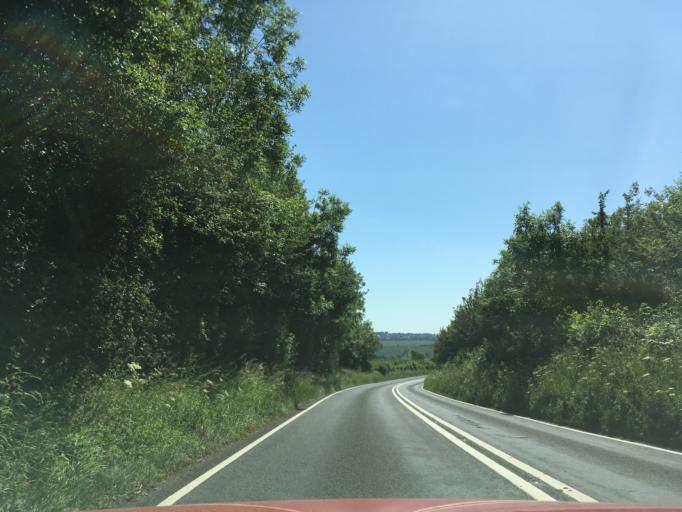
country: GB
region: England
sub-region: Oxfordshire
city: Chipping Norton
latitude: 51.9543
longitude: -1.5970
